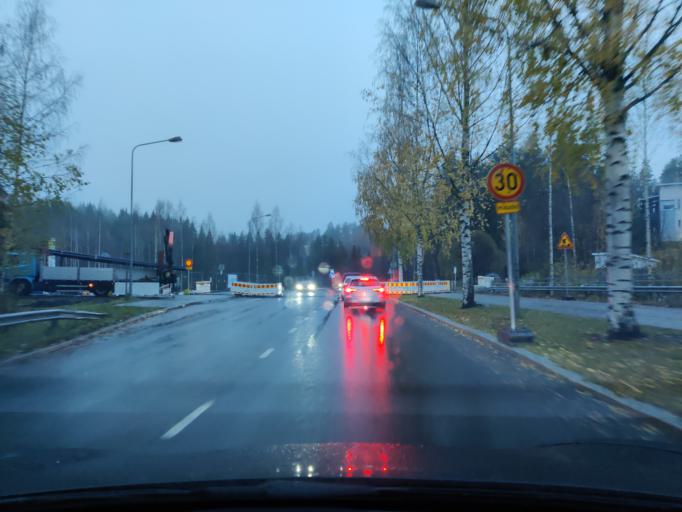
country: FI
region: Northern Savo
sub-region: Kuopio
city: Kuopio
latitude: 62.8448
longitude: 27.6550
